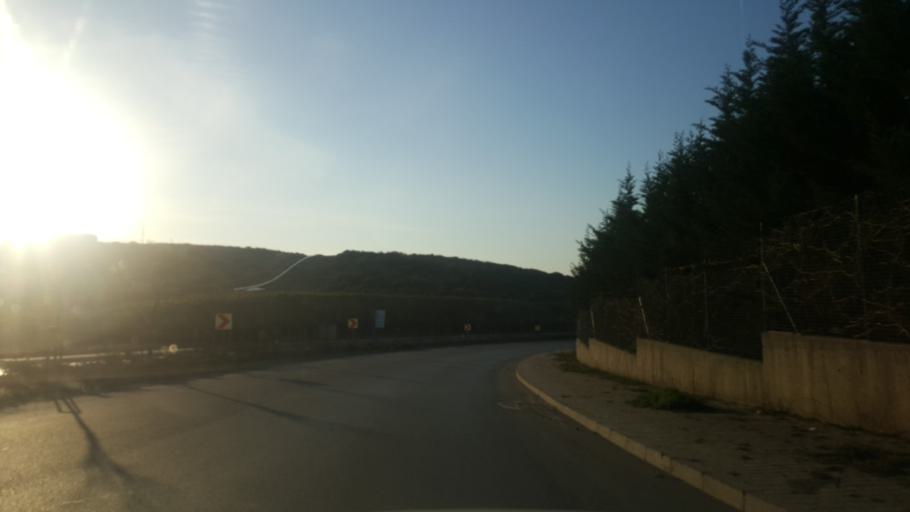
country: TR
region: Kocaeli
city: Tavsancil
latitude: 40.8172
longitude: 29.5653
